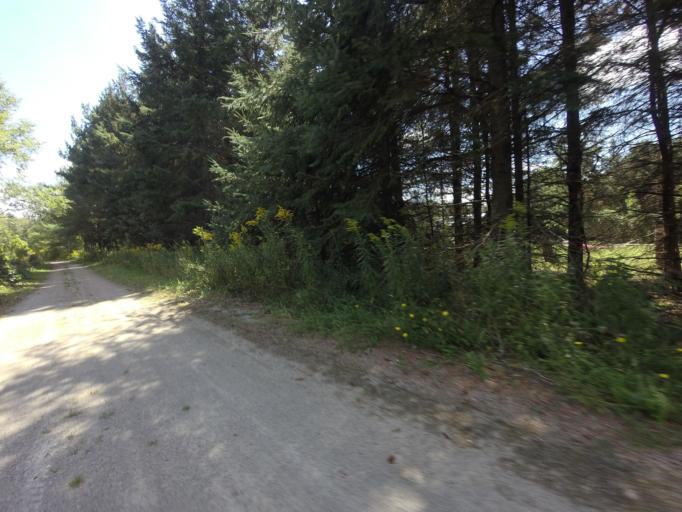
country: CA
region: Ontario
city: Orangeville
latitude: 43.7797
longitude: -80.1265
